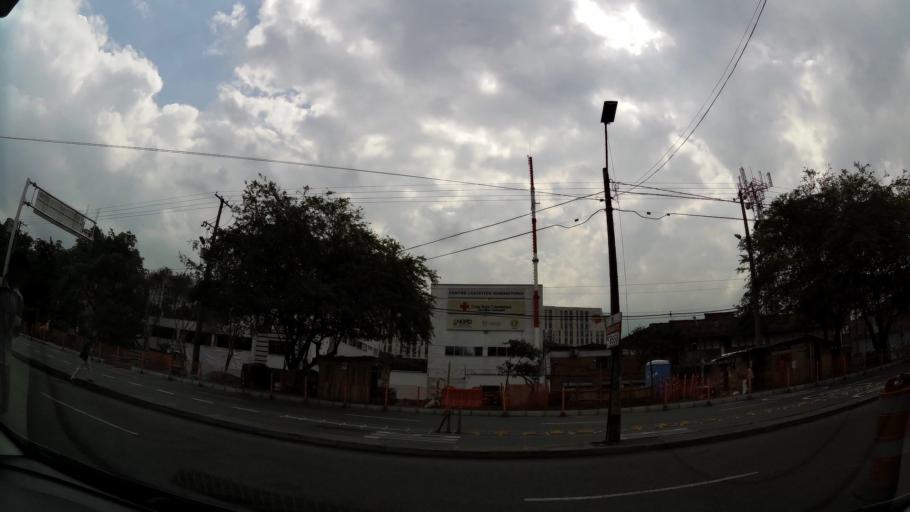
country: CO
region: Antioquia
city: Medellin
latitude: 6.2284
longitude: -75.5777
